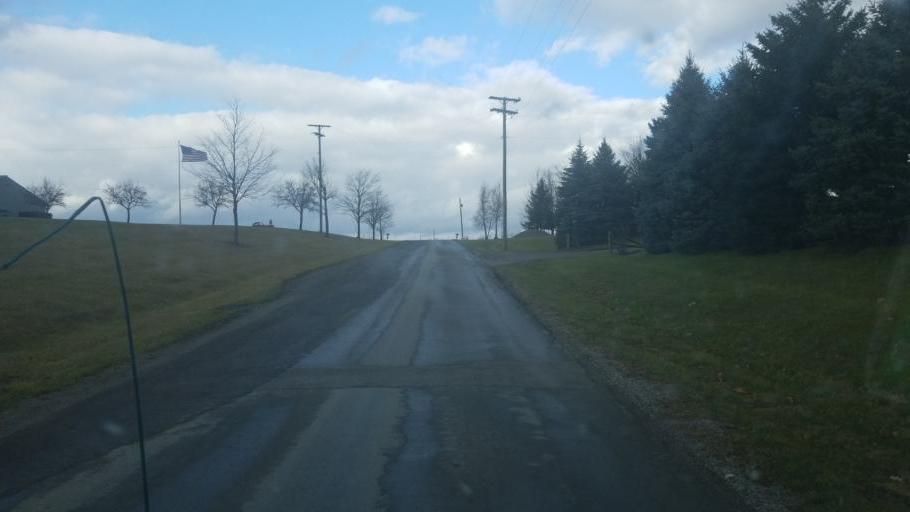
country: US
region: Ohio
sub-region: Wyandot County
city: Upper Sandusky
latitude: 40.7842
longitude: -83.2316
